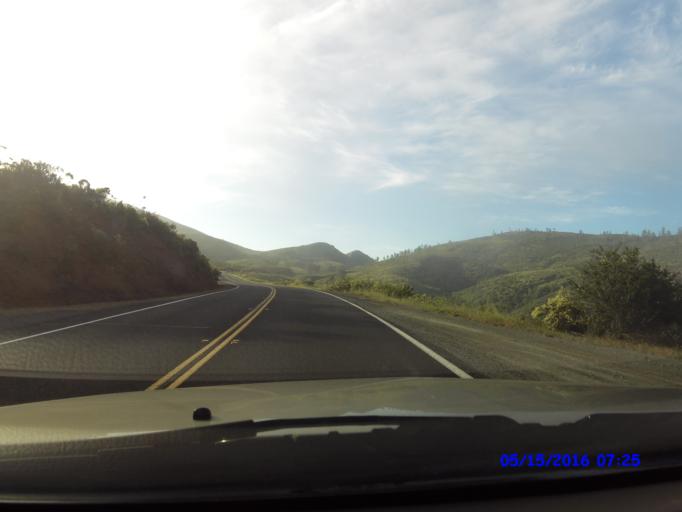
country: US
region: California
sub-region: Tuolumne County
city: Tuolumne City
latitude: 37.7633
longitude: -120.2581
